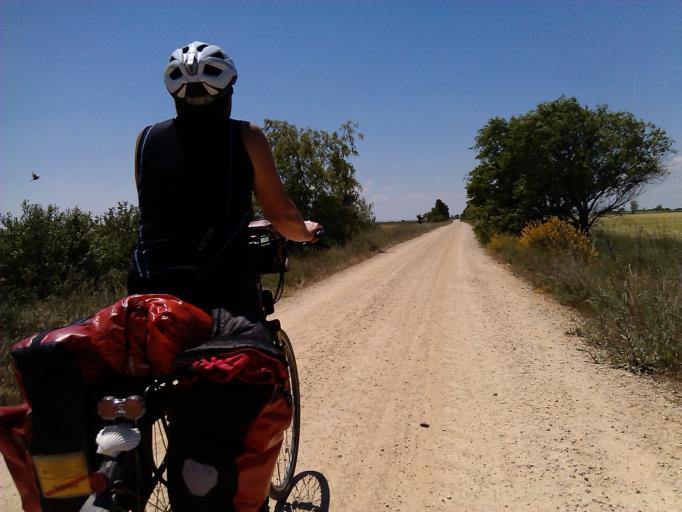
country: ES
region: Castille and Leon
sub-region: Provincia de Palencia
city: Villaturde
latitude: 42.3414
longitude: -4.6948
